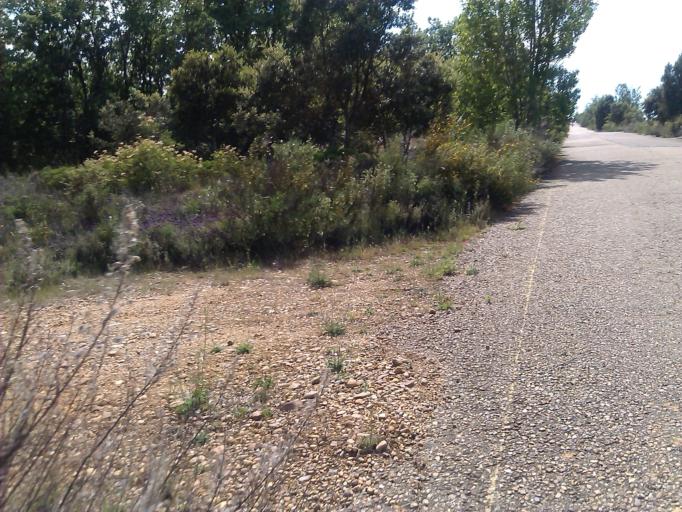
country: ES
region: Castille and Leon
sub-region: Provincia de Leon
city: San Justo de la Vega
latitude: 42.4479
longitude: -5.9750
